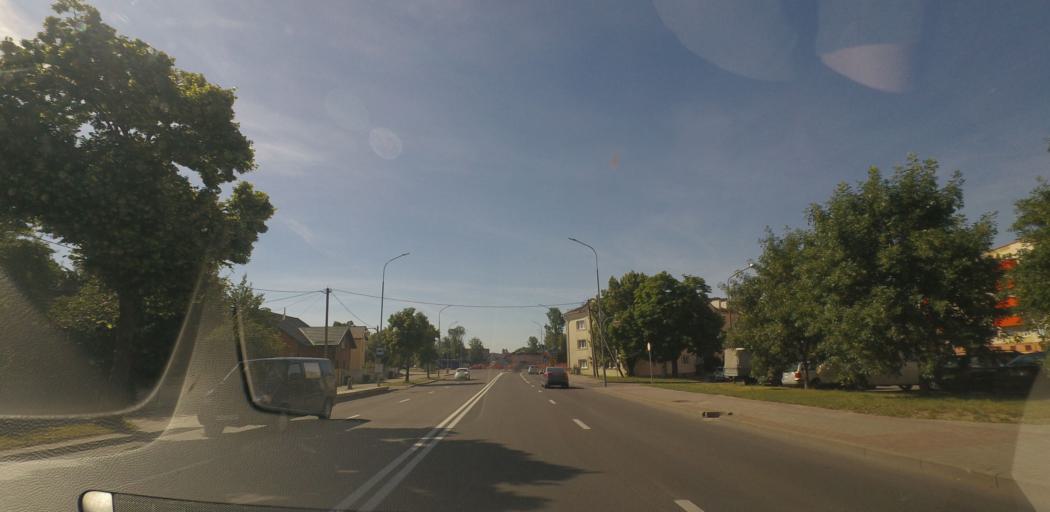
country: BY
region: Grodnenskaya
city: Hrodna
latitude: 53.6730
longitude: 23.8536
